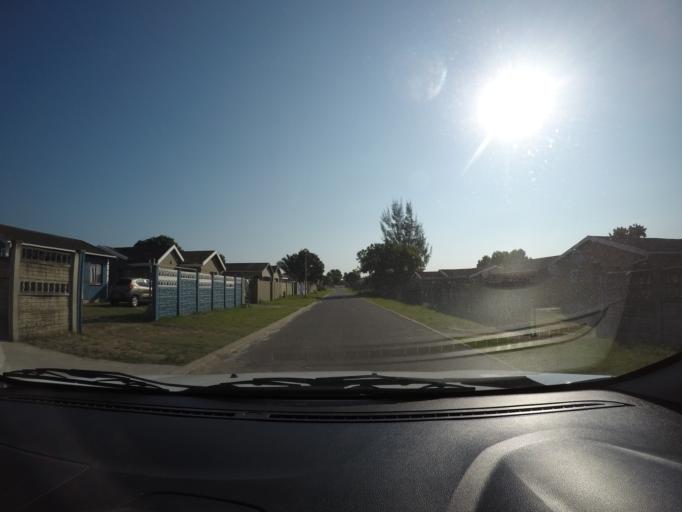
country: ZA
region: KwaZulu-Natal
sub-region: uThungulu District Municipality
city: Richards Bay
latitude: -28.7131
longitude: 32.0407
